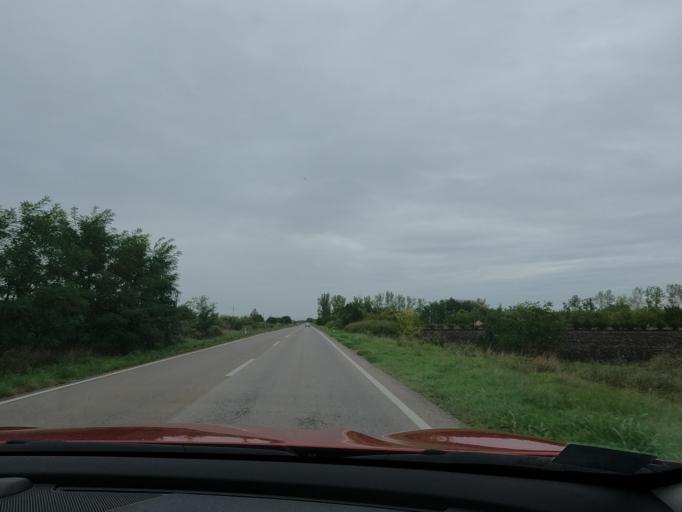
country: RS
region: Autonomna Pokrajina Vojvodina
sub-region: Severnobanatski Okrug
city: Kikinda
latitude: 45.7716
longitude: 20.4252
